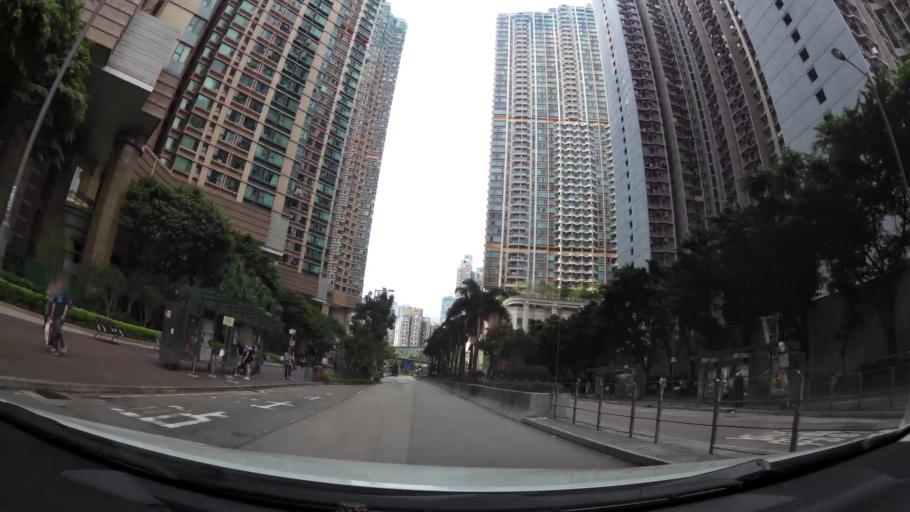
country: HK
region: Sham Shui Po
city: Sham Shui Po
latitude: 22.3160
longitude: 114.1638
